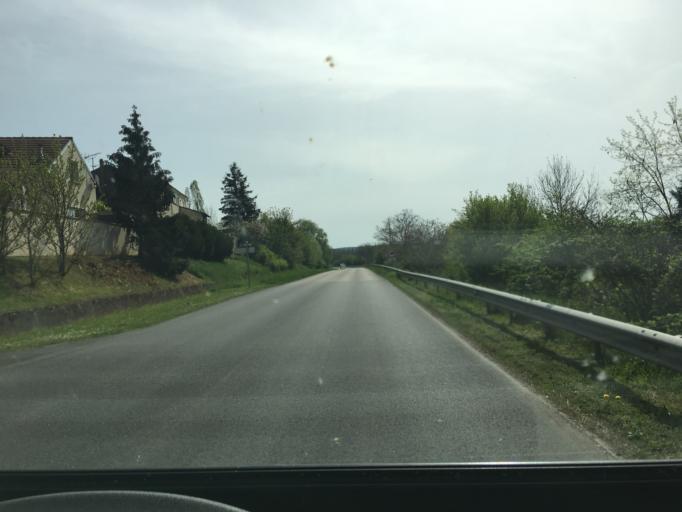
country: FR
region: Lorraine
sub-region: Departement de Meurthe-et-Moselle
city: Chavigny
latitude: 48.6125
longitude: 6.1243
